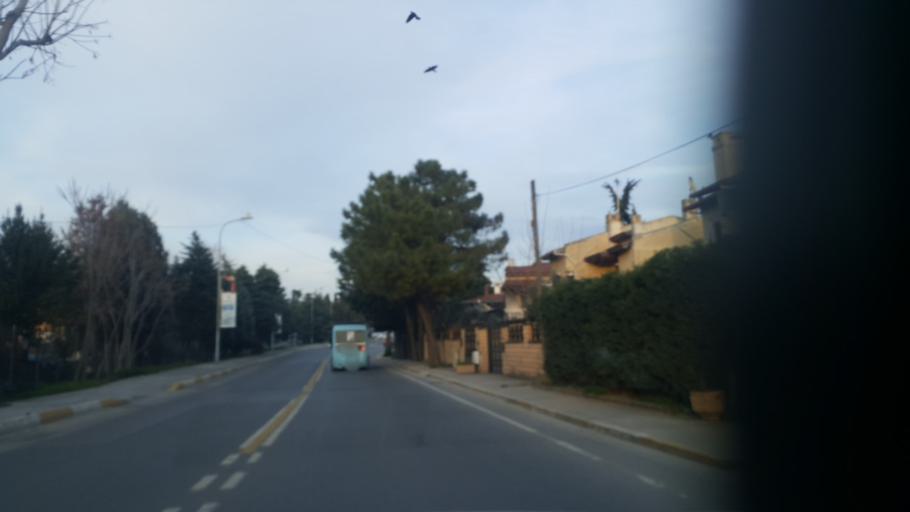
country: TR
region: Istanbul
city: Icmeler
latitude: 40.8177
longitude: 29.2750
